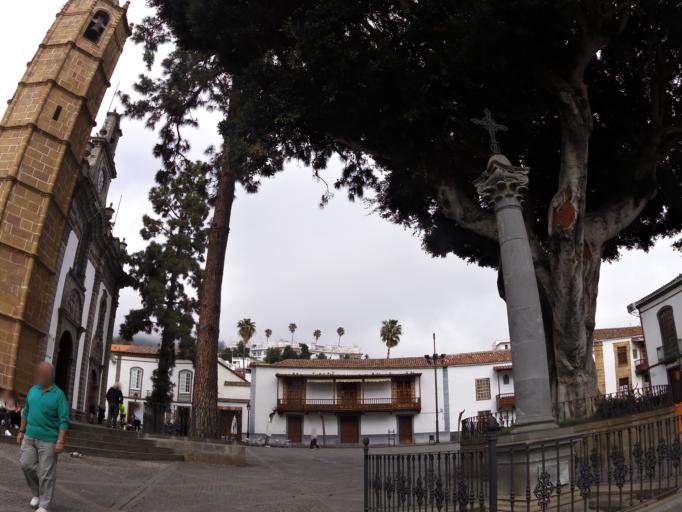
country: ES
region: Canary Islands
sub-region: Provincia de Las Palmas
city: Teror
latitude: 28.0595
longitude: -15.5473
